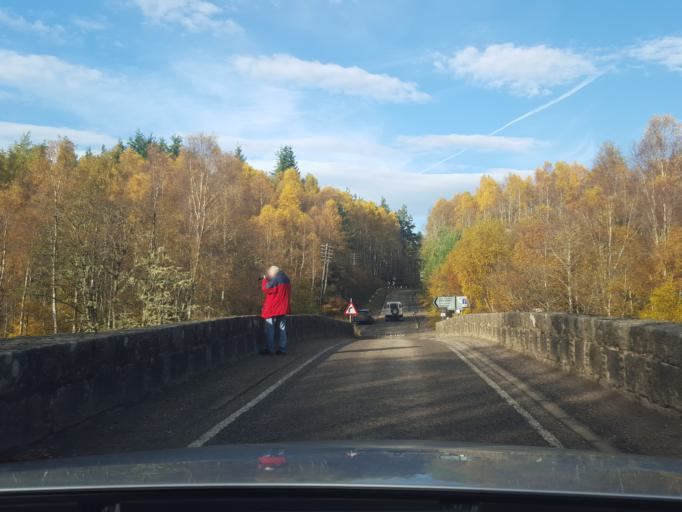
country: GB
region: Scotland
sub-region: Highland
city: Spean Bridge
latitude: 57.1758
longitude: -4.7985
